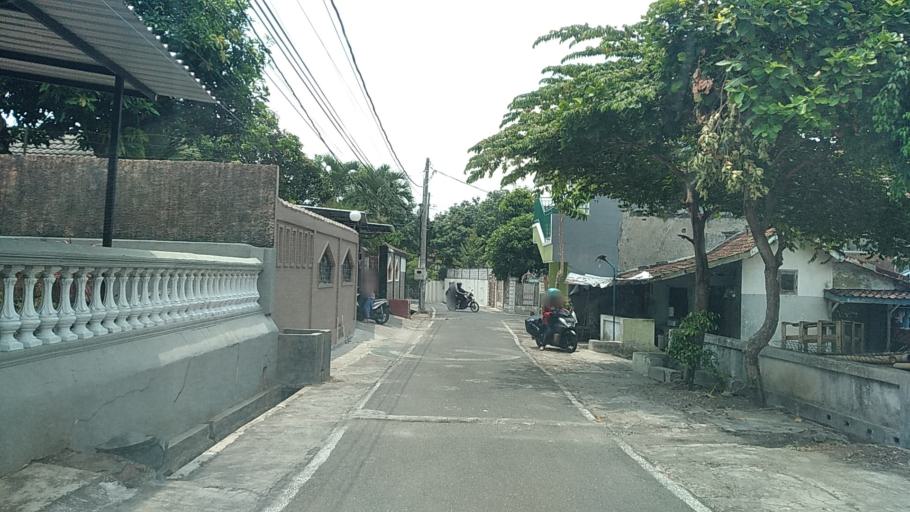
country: ID
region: Central Java
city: Semarang
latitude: -7.0458
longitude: 110.4226
